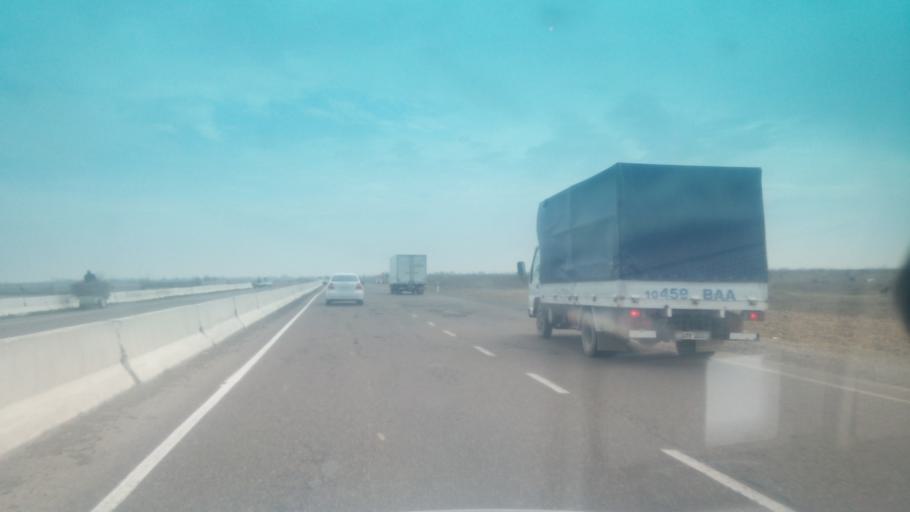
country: KZ
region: Ongtustik Qazaqstan
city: Myrzakent
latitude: 40.5125
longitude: 68.4921
